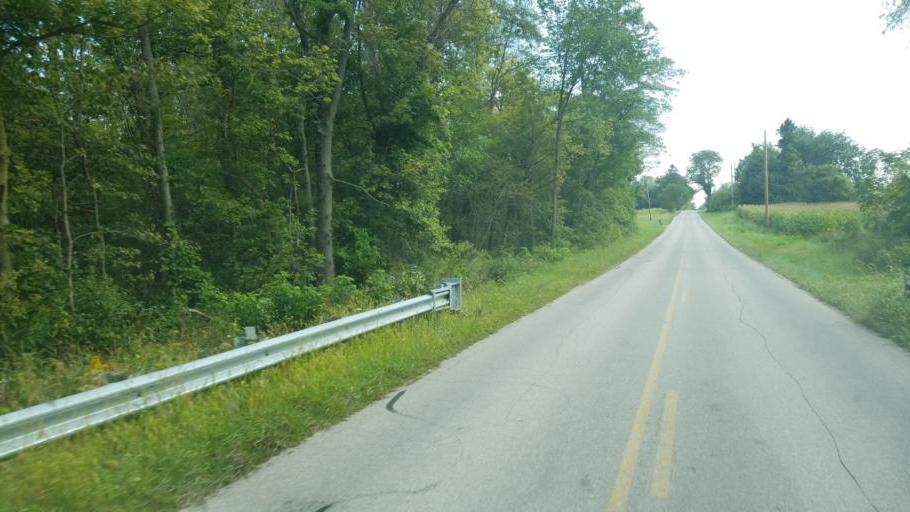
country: US
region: Ohio
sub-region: Seneca County
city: Tiffin
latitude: 41.0659
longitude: -83.1207
